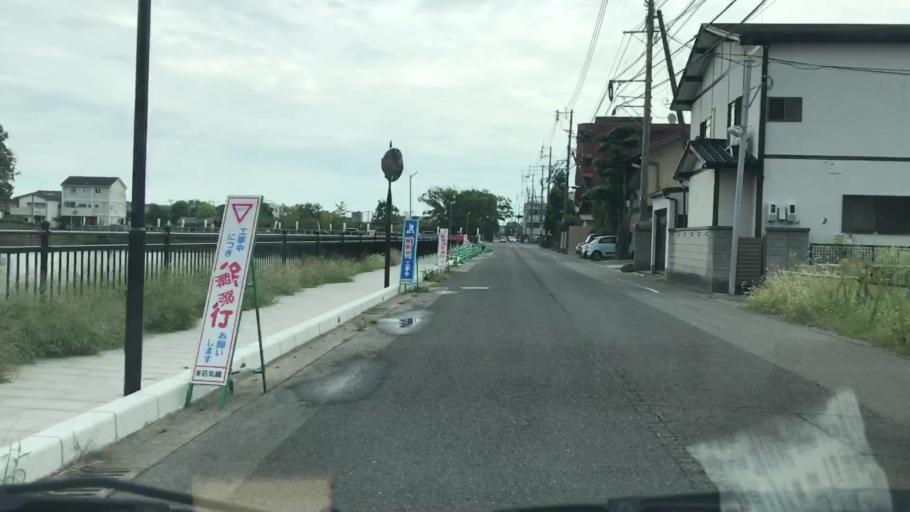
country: JP
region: Saga Prefecture
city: Saga-shi
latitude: 33.2470
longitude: 130.2958
